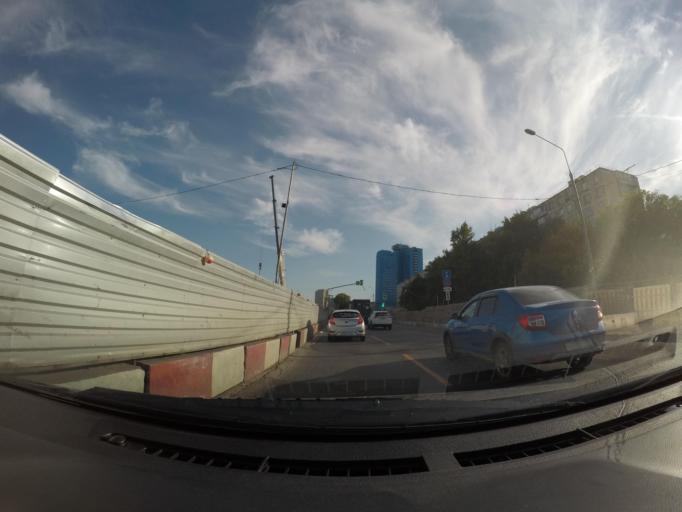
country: RU
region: Moscow
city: Likhobory
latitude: 55.8298
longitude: 37.5726
